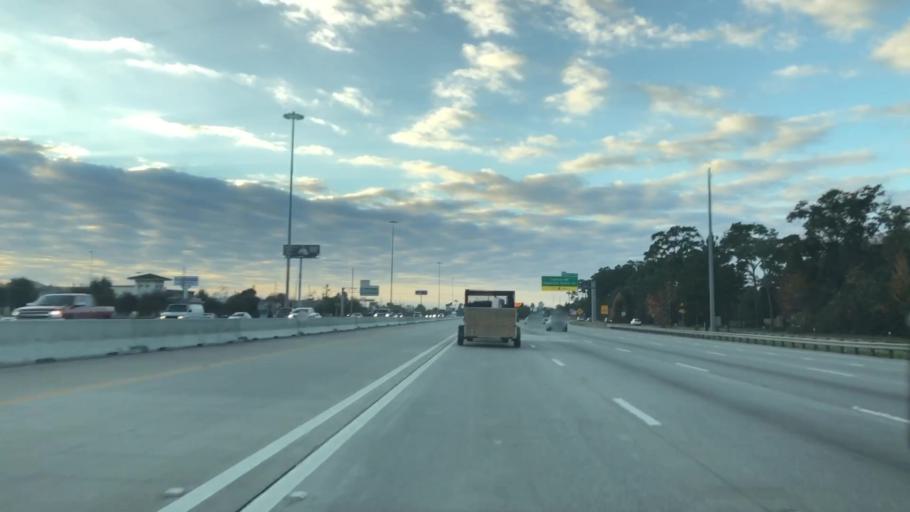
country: US
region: Texas
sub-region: Montgomery County
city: Shenandoah
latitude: 30.1978
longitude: -95.4547
